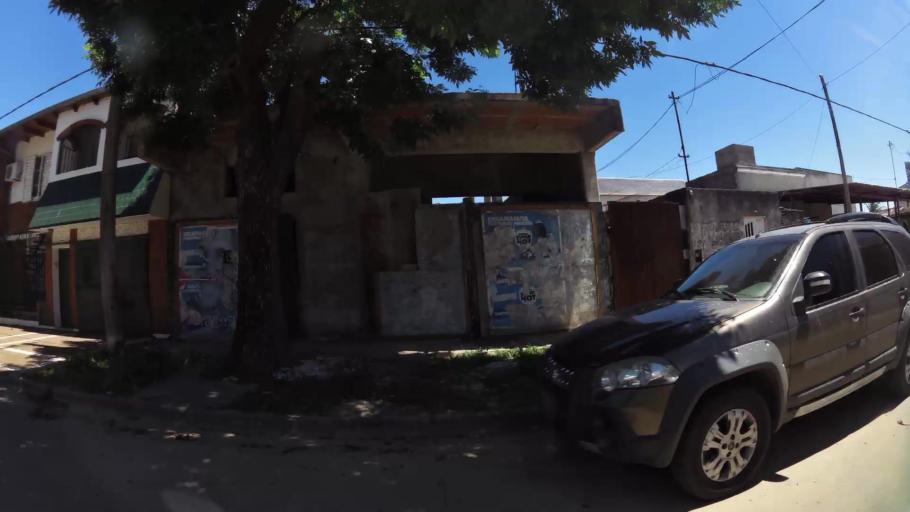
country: AR
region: Santa Fe
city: Santa Fe de la Vera Cruz
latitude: -31.6489
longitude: -60.7267
